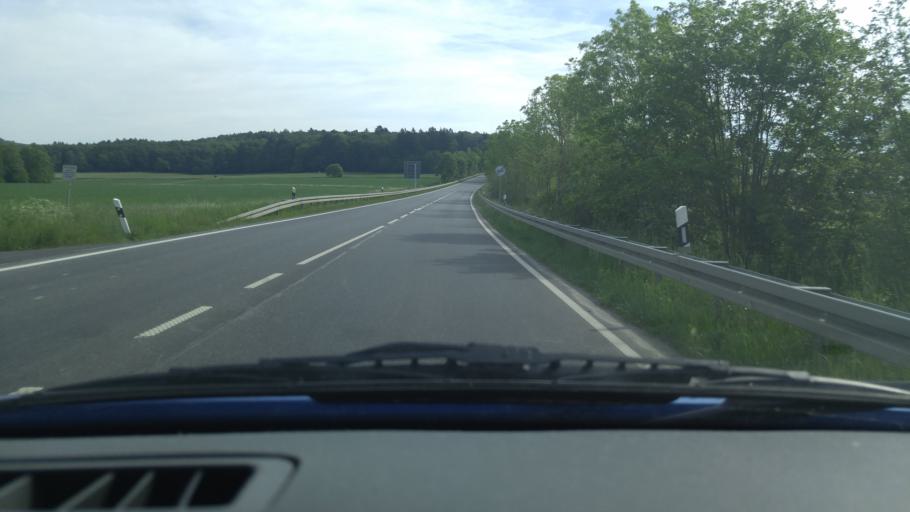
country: DE
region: Hesse
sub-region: Regierungsbezirk Giessen
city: Schotten
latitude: 50.4770
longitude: 9.0827
